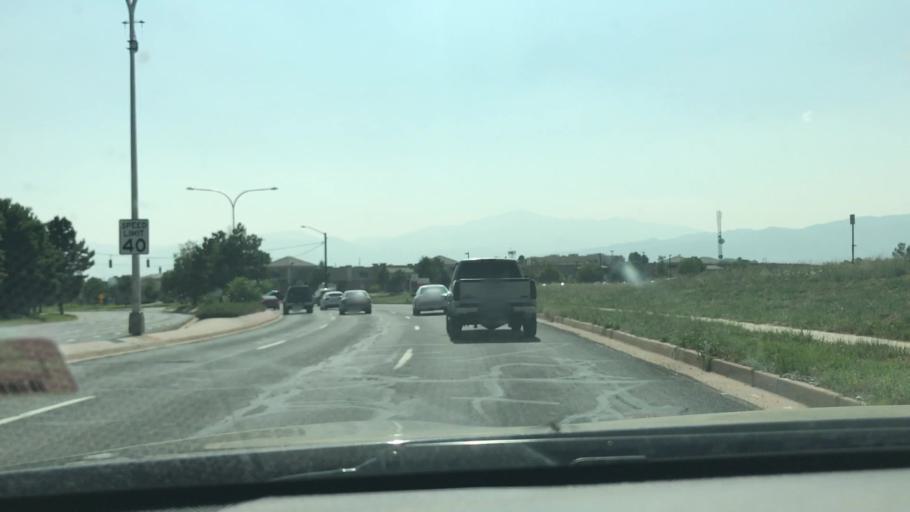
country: US
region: Colorado
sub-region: El Paso County
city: Black Forest
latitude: 38.9602
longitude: -104.7631
